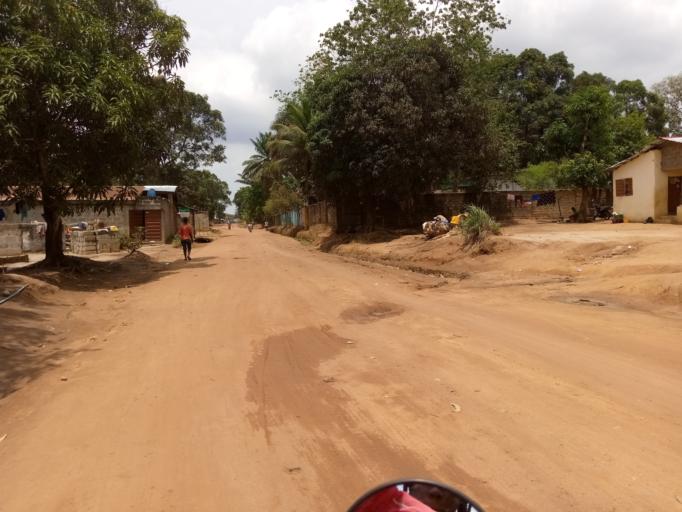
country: SL
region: Western Area
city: Waterloo
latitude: 8.3321
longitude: -13.0412
